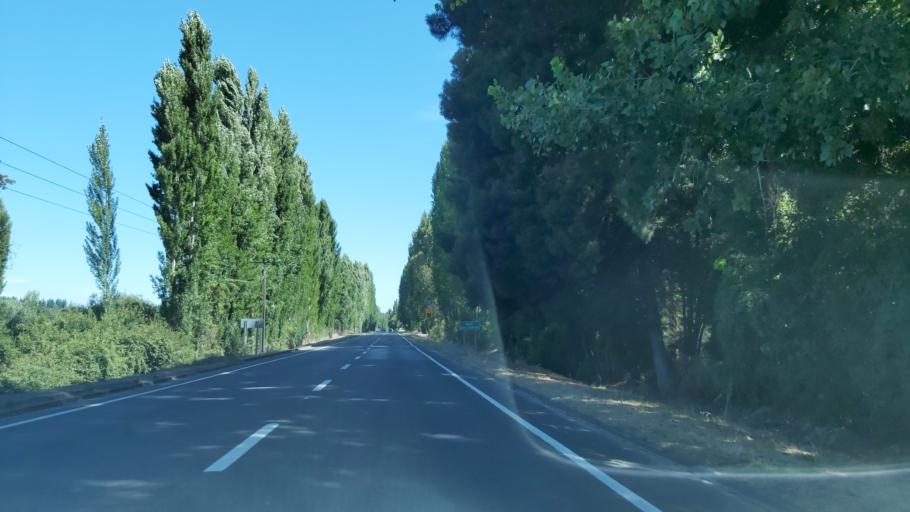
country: CL
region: Biobio
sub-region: Provincia de Concepcion
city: Lota
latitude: -37.1437
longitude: -72.9781
